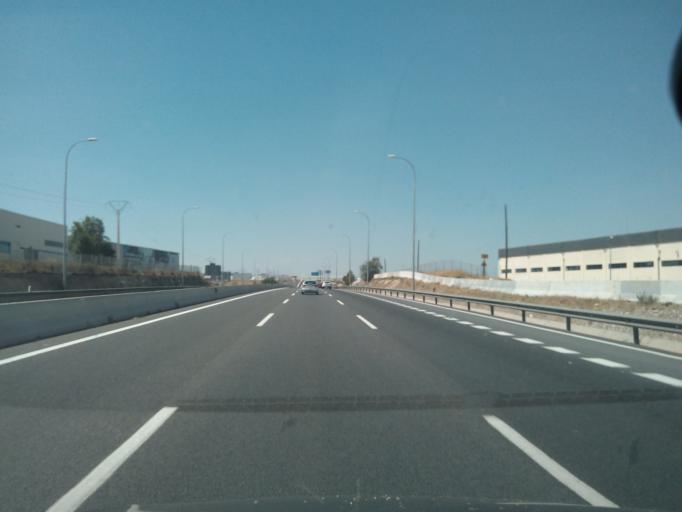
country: ES
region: Castille-La Mancha
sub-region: Province of Toledo
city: Sesena
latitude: 40.1151
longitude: -3.6516
